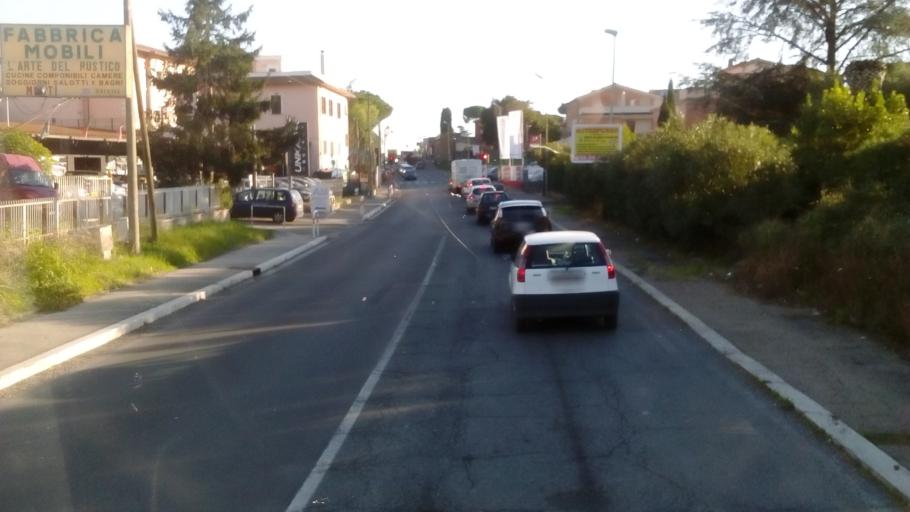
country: IT
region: Latium
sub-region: Citta metropolitana di Roma Capitale
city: Pavona
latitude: 41.7286
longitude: 12.6166
